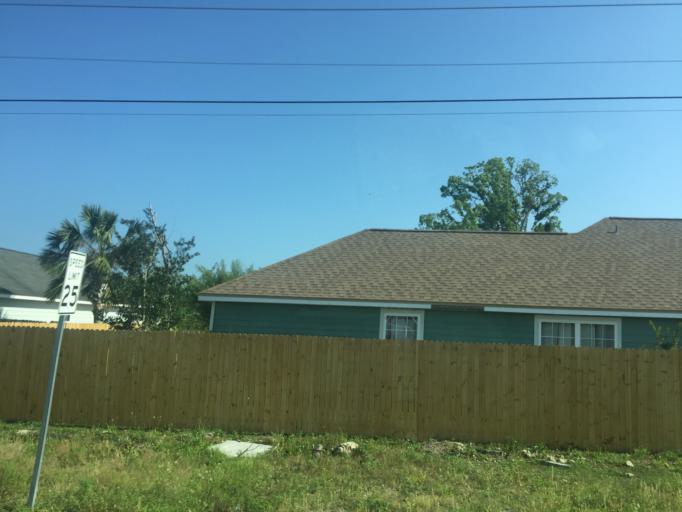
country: US
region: Florida
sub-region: Bay County
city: Springfield
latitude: 30.1603
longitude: -85.5948
